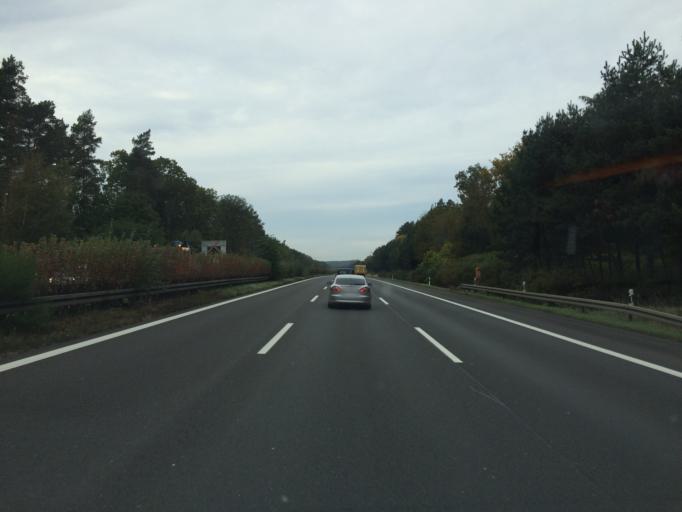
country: DE
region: Brandenburg
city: Michendorf
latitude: 52.3036
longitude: 13.0018
